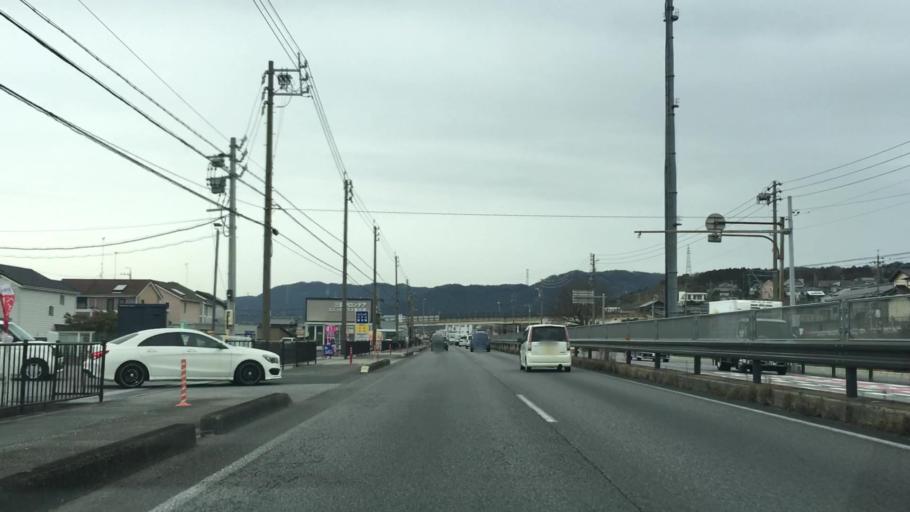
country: JP
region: Aichi
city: Kozakai-cho
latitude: 34.8462
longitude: 137.3208
